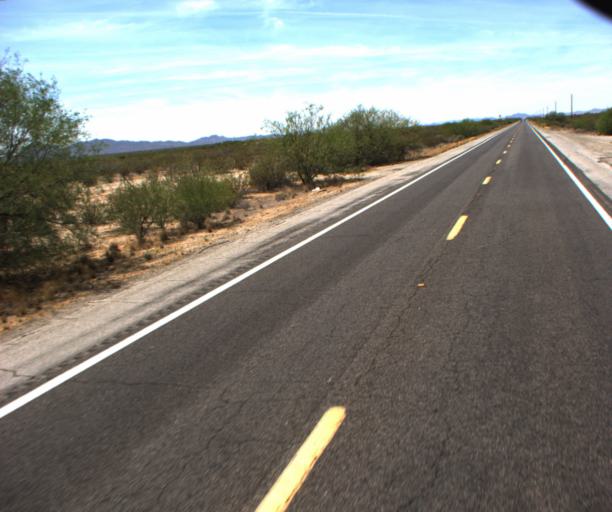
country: US
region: Arizona
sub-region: La Paz County
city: Salome
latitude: 33.8688
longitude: -113.3975
